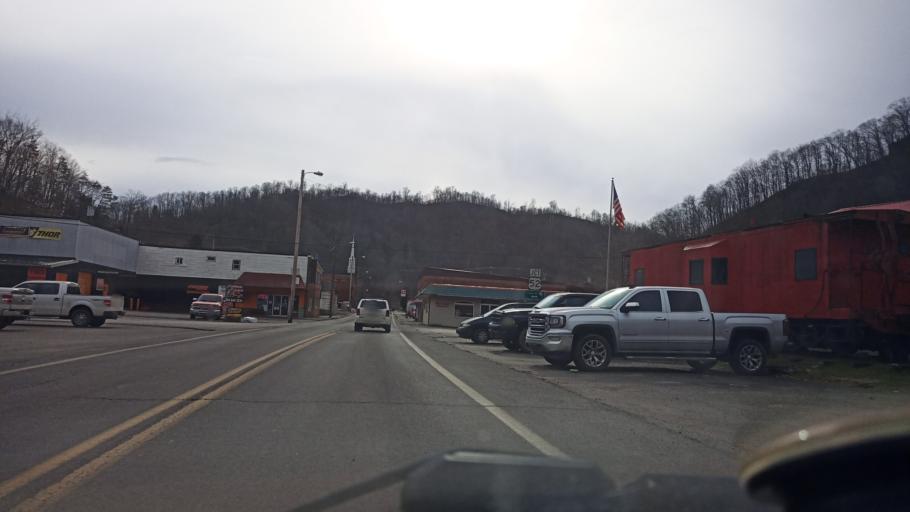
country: US
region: West Virginia
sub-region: Mingo County
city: Gilbert Creek
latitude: 37.6168
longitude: -81.8663
